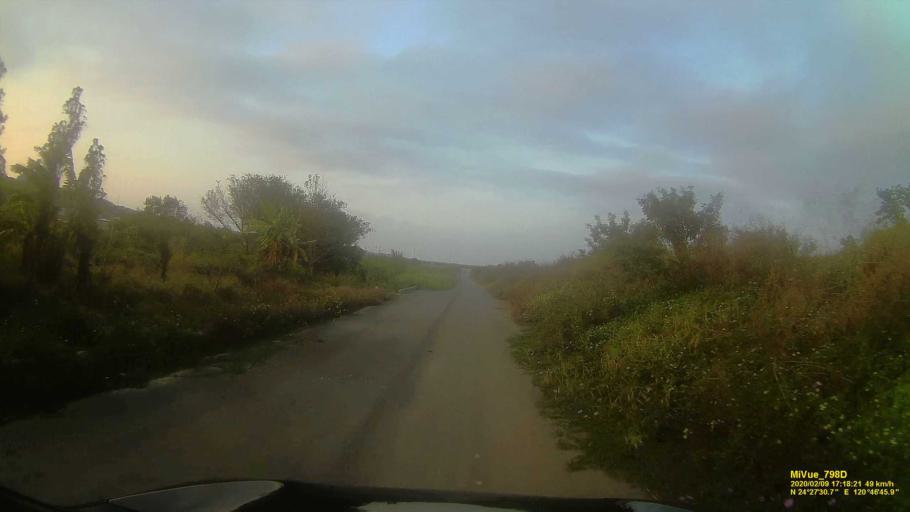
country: TW
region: Taiwan
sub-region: Miaoli
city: Miaoli
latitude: 24.4588
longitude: 120.7794
